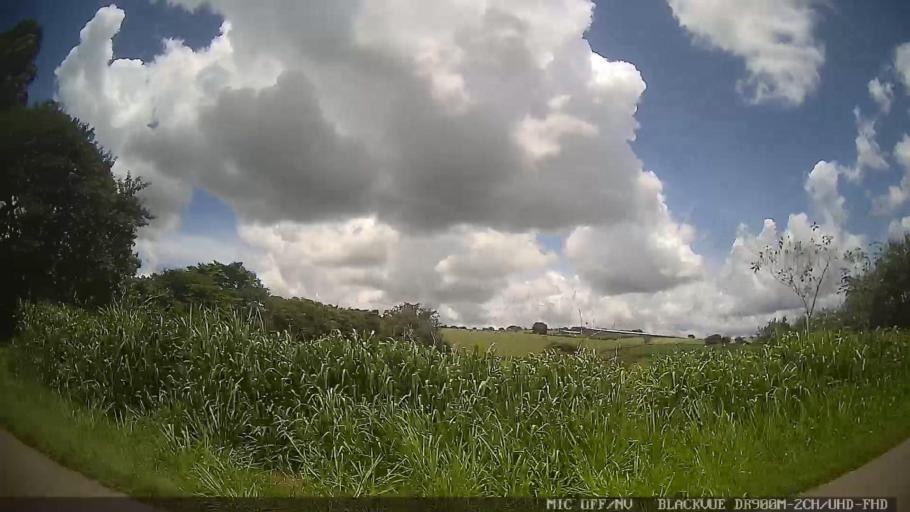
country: BR
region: Sao Paulo
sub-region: Amparo
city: Amparo
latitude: -22.8361
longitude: -46.6683
